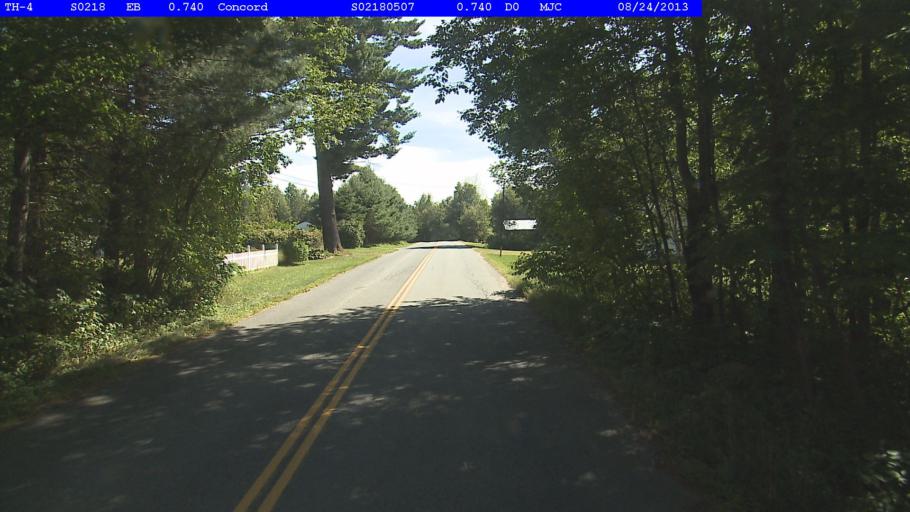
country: US
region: New Hampshire
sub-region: Grafton County
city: Littleton
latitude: 44.4550
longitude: -71.7703
